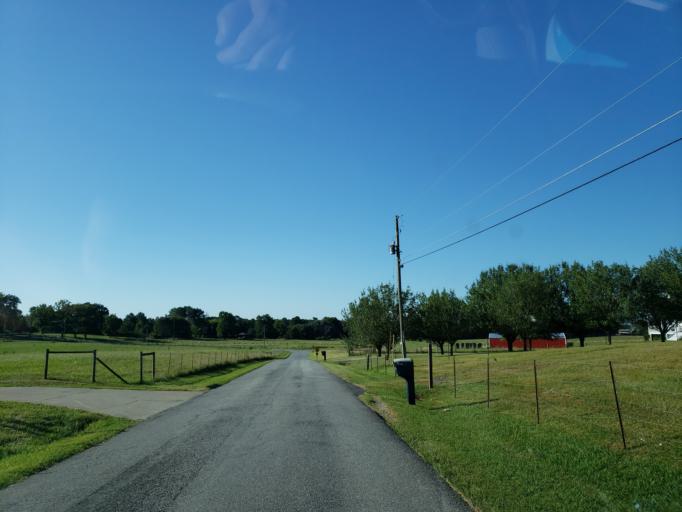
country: US
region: Georgia
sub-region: Bartow County
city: Euharlee
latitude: 34.1097
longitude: -84.9912
